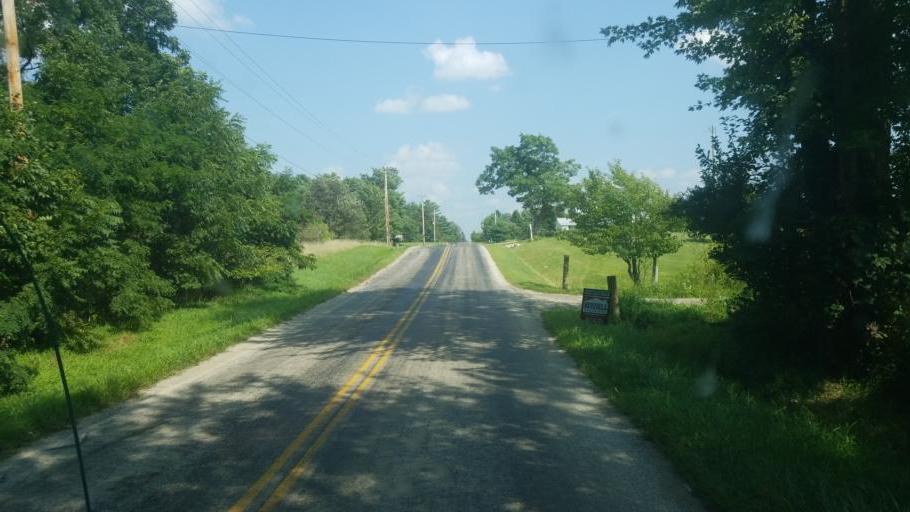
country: US
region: Ohio
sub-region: Lorain County
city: Wellington
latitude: 41.0577
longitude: -82.2523
